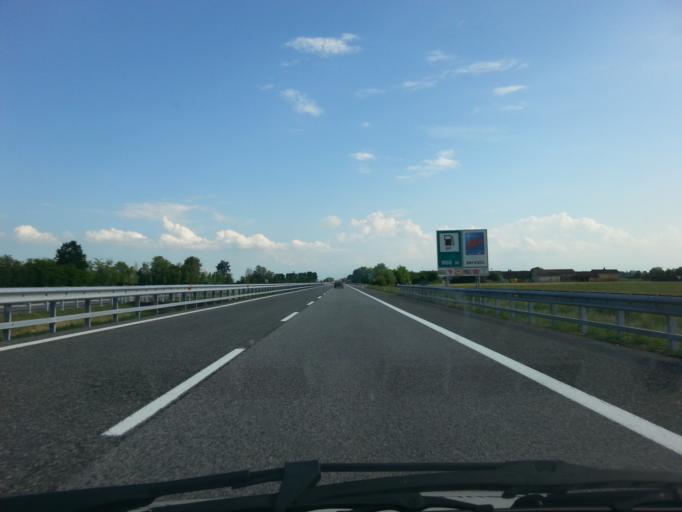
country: IT
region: Piedmont
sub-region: Provincia di Cuneo
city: Sanfre
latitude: 44.7154
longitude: 7.7598
